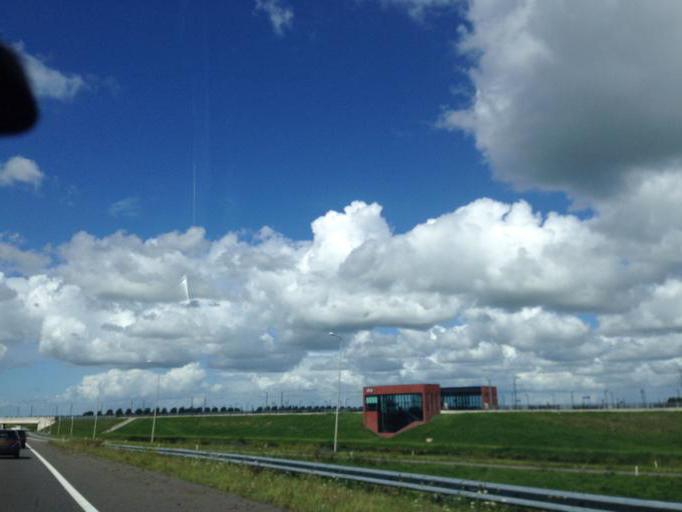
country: NL
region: Overijssel
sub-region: Gemeente Kampen
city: Kampen
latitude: 52.5311
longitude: 5.9137
